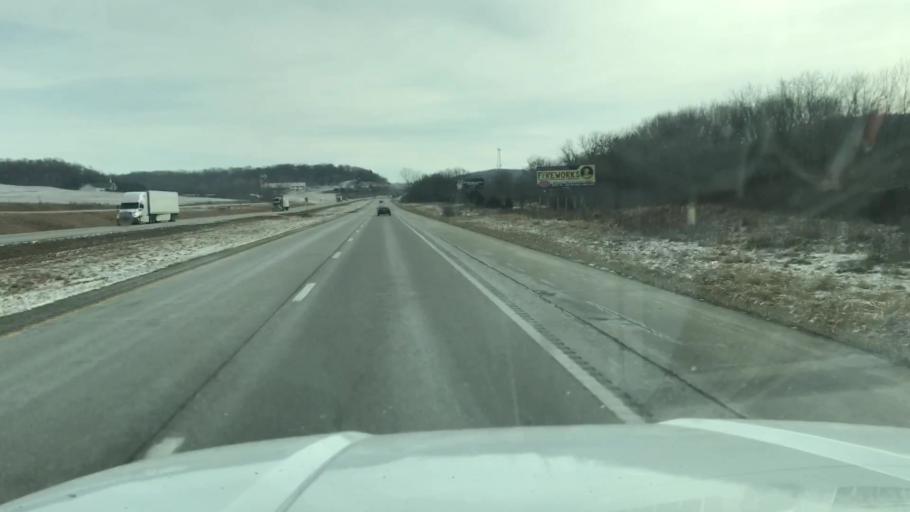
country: US
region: Missouri
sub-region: Andrew County
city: Savannah
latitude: 39.9699
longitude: -94.9857
